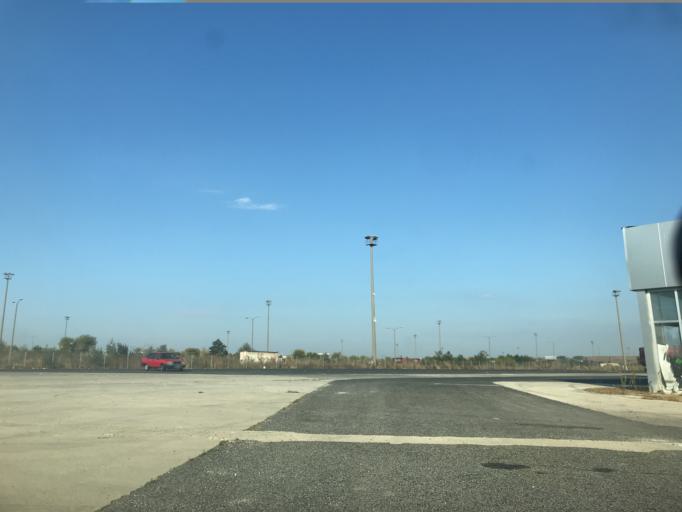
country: TR
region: Tekirdag
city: Marmaracik
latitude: 41.2877
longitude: 27.7866
